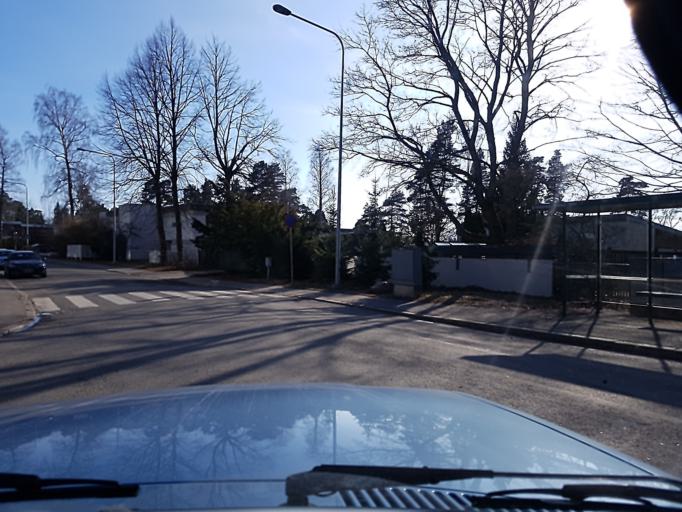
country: FI
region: Uusimaa
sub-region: Helsinki
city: Teekkarikylae
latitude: 60.1684
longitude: 24.8575
